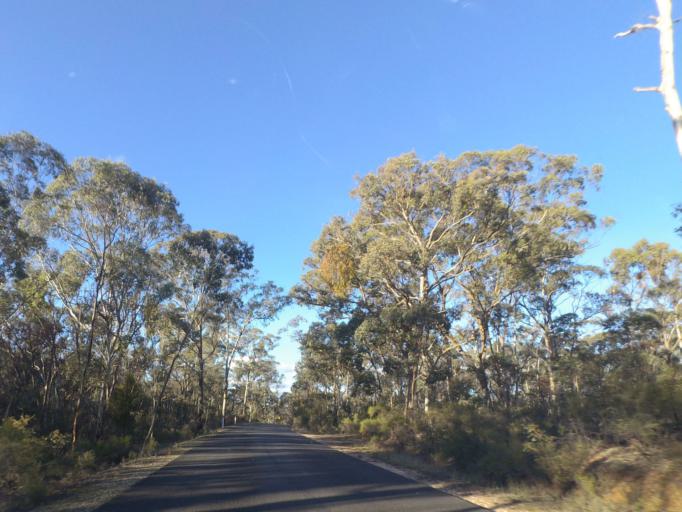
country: AU
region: Victoria
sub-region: Mount Alexander
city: Castlemaine
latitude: -37.1418
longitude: 144.1989
